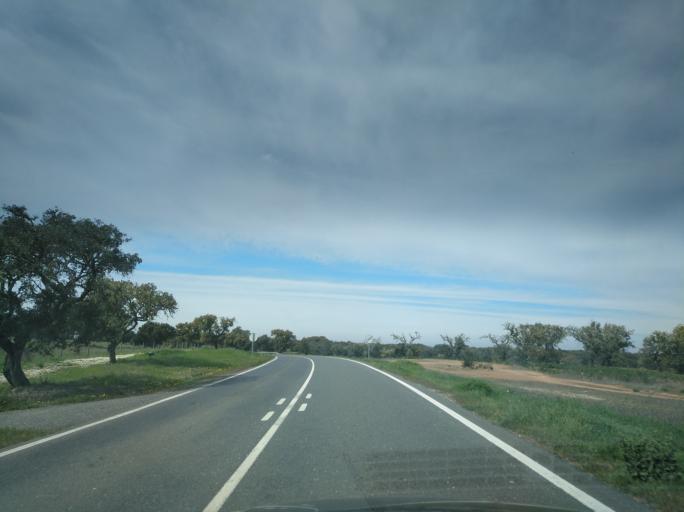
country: PT
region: Beja
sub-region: Mertola
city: Mertola
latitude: 37.7494
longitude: -7.8013
